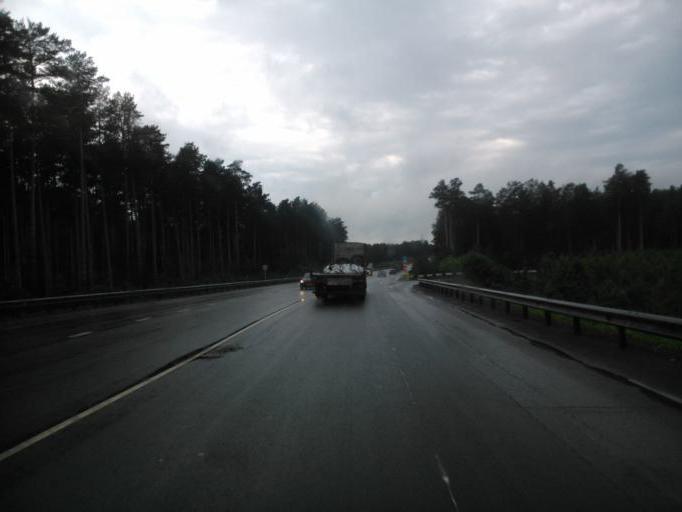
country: RU
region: Sverdlovsk
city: Beryozovsky
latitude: 56.8979
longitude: 60.7614
